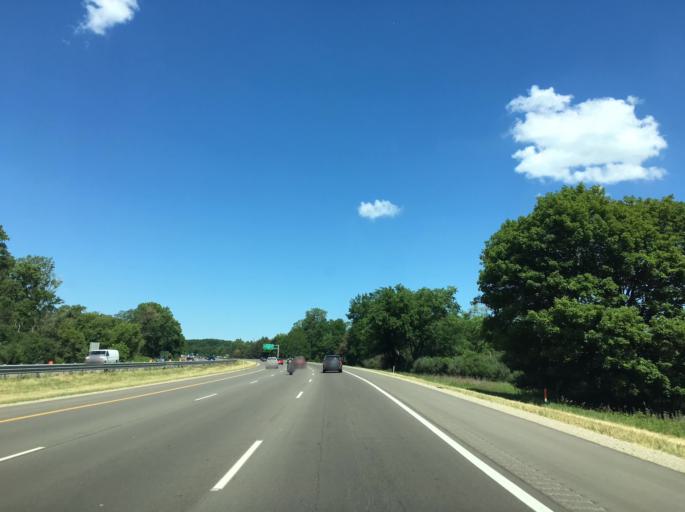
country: US
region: Michigan
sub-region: Oakland County
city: Clarkston
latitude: 42.7250
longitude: -83.3546
